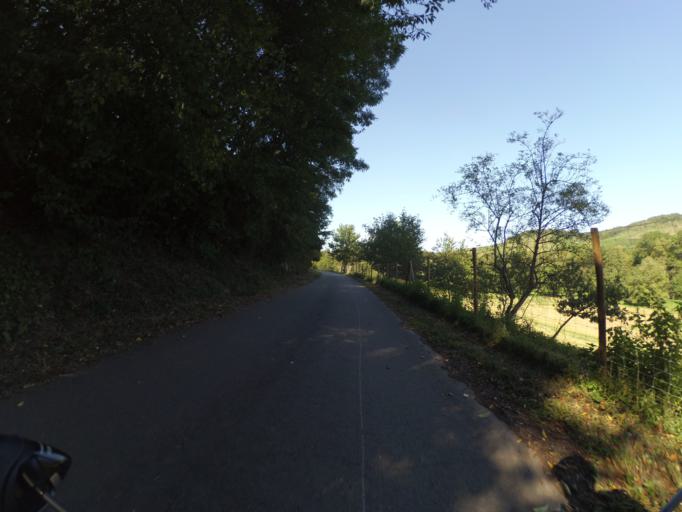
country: DE
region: Rheinland-Pfalz
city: Thornich
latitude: 49.8472
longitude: 6.8384
